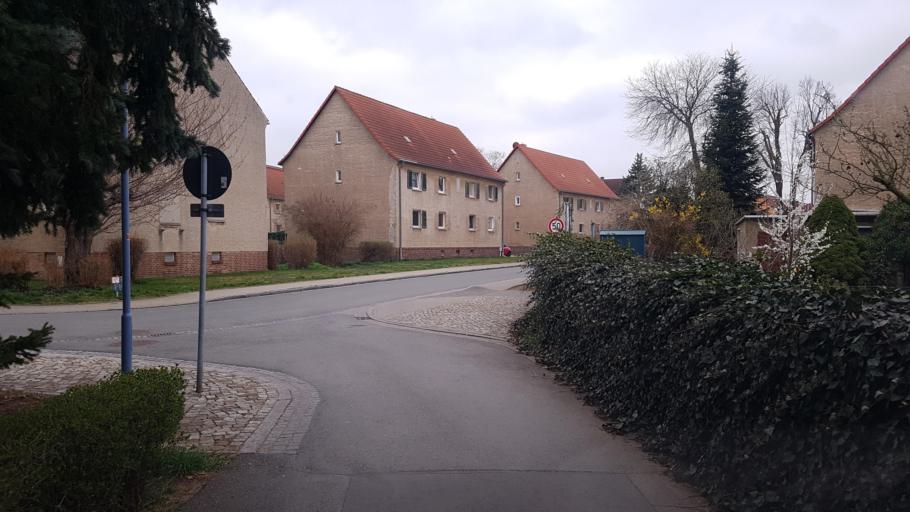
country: DE
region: Saxony
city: Nauwalde
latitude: 51.4221
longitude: 13.4513
